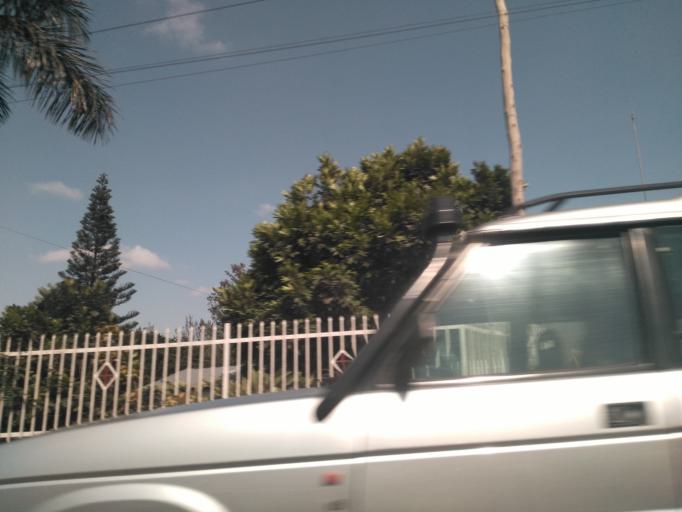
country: TZ
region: Arusha
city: Arusha
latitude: -3.3715
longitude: 36.6934
